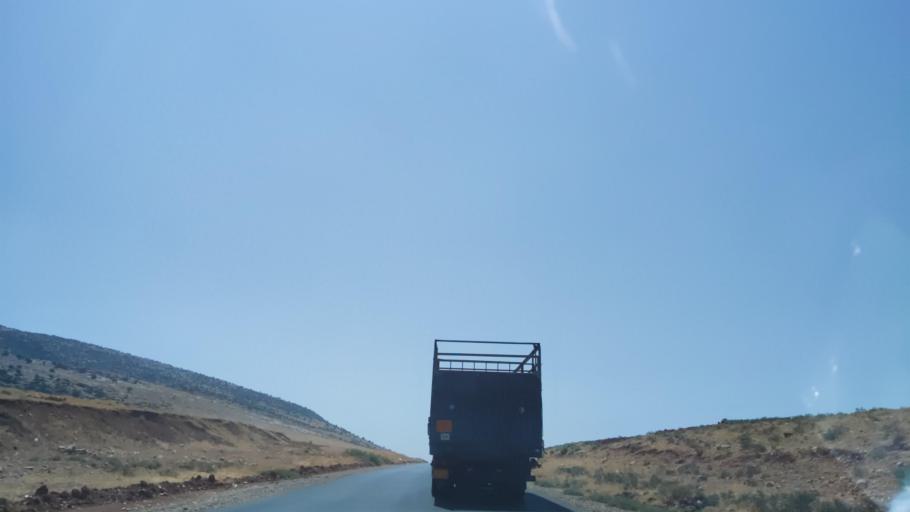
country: IQ
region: Arbil
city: Shaqlawah
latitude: 36.5974
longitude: 44.3171
